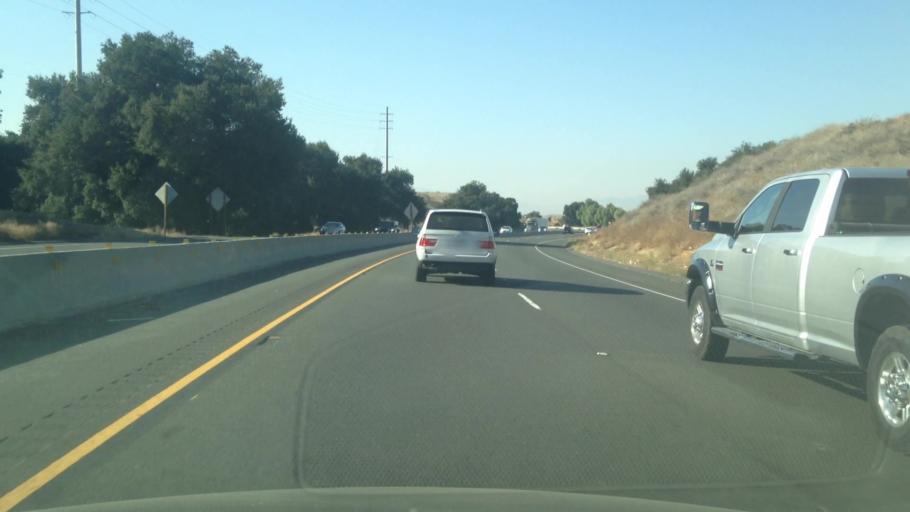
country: US
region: California
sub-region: Riverside County
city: Beaumont
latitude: 33.9358
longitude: -117.0375
